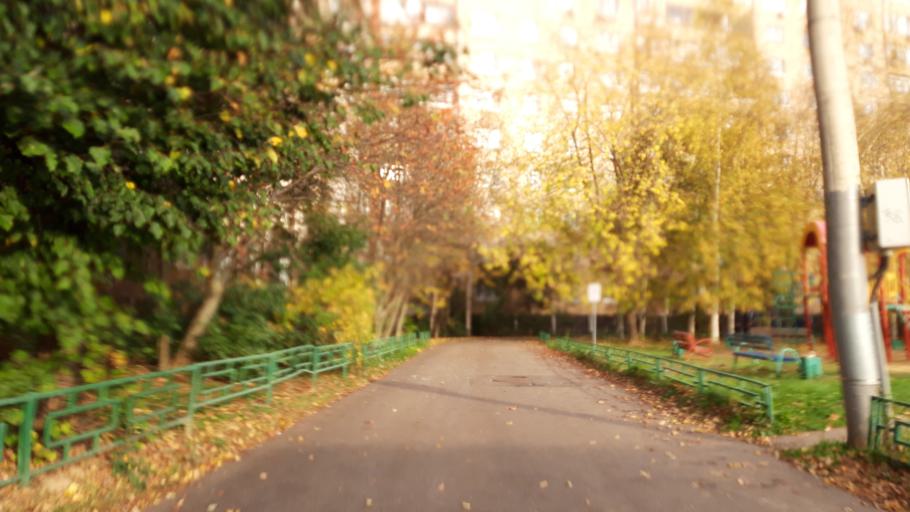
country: RU
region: Moscow
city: Zelenograd
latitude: 55.9949
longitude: 37.1729
